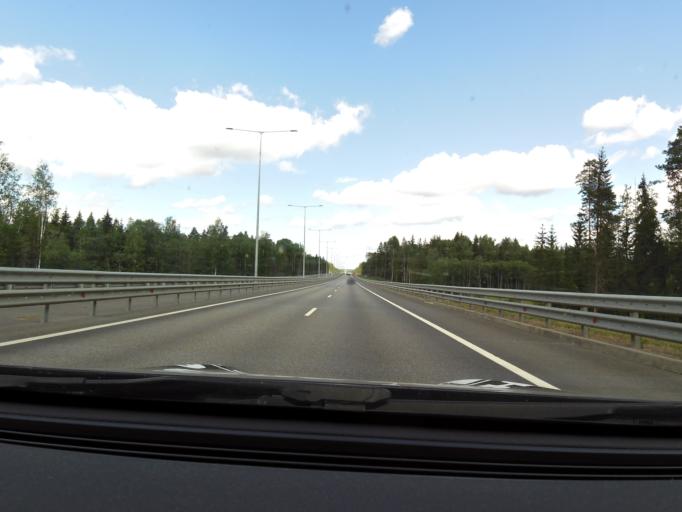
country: RU
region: Tverskaya
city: Vydropuzhsk
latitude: 57.2999
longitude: 34.7728
